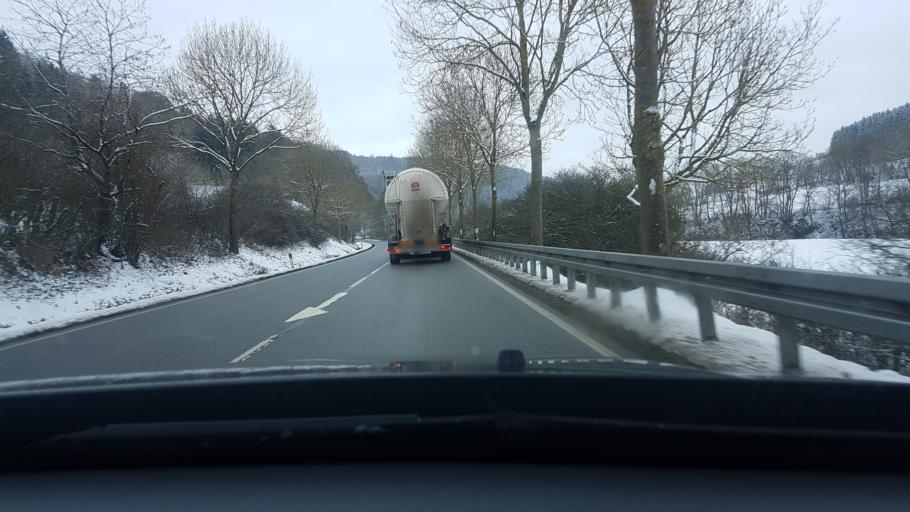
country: DE
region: North Rhine-Westphalia
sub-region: Regierungsbezirk Arnsberg
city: Medebach
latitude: 51.2918
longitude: 8.7397
